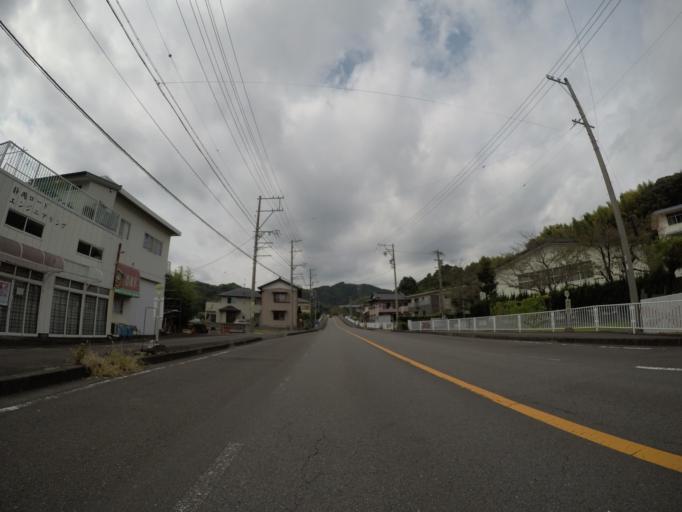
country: JP
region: Shizuoka
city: Fujieda
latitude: 34.8813
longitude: 138.2176
